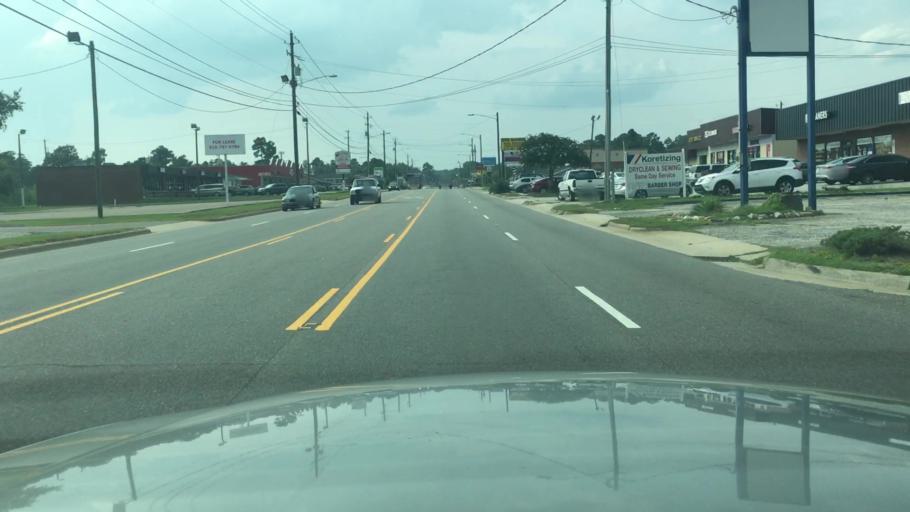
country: US
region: North Carolina
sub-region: Cumberland County
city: Fort Bragg
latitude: 35.1021
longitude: -78.9916
